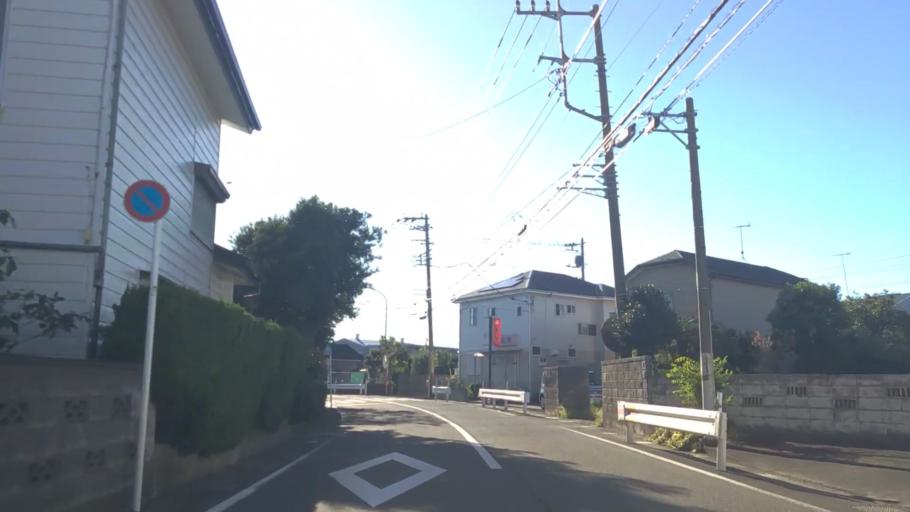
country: JP
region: Kanagawa
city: Atsugi
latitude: 35.3880
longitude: 139.3679
